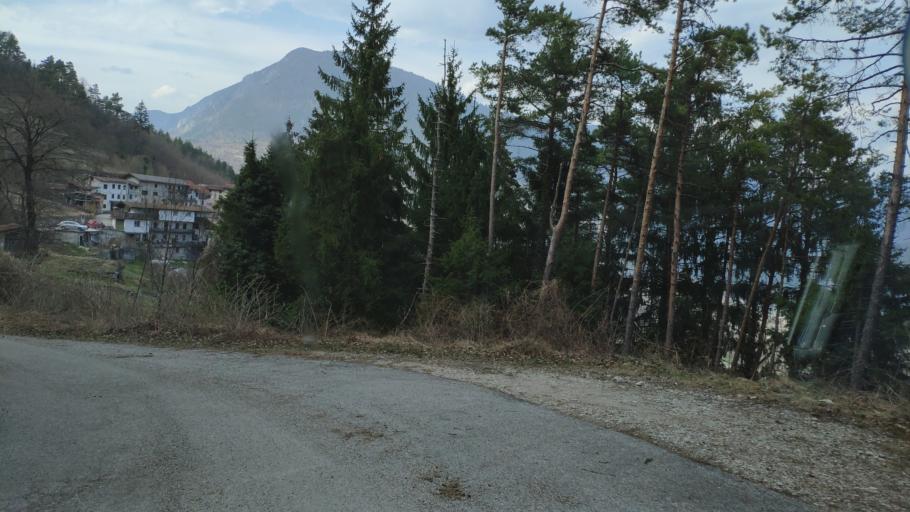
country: IT
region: Veneto
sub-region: Provincia di Vicenza
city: Enego
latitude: 45.9532
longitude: 11.7044
